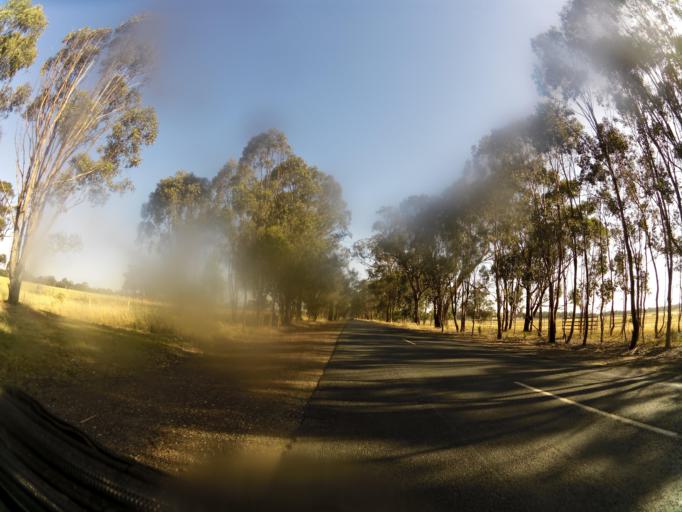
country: AU
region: Victoria
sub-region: Murrindindi
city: Kinglake West
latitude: -36.9766
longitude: 145.1102
